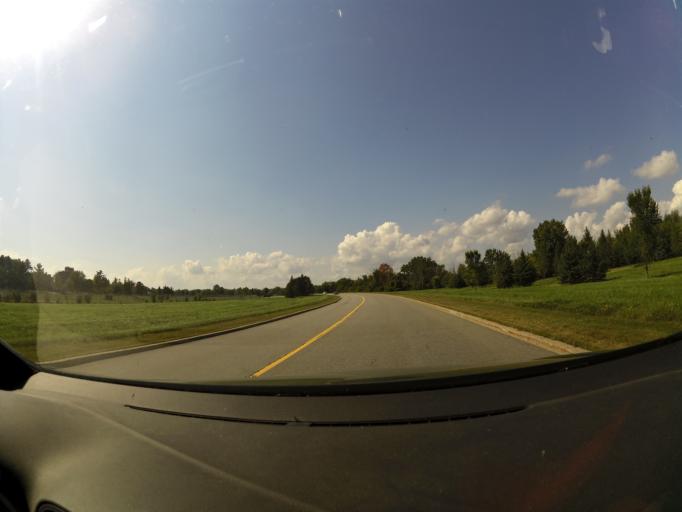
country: CA
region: Quebec
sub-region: Outaouais
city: Gatineau
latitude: 45.4599
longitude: -75.6536
